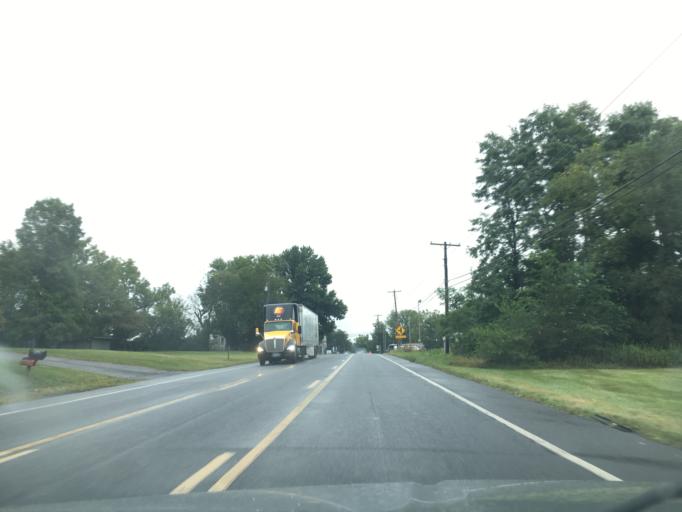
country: US
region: Pennsylvania
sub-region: Berks County
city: Kutztown
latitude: 40.4980
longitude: -75.8030
